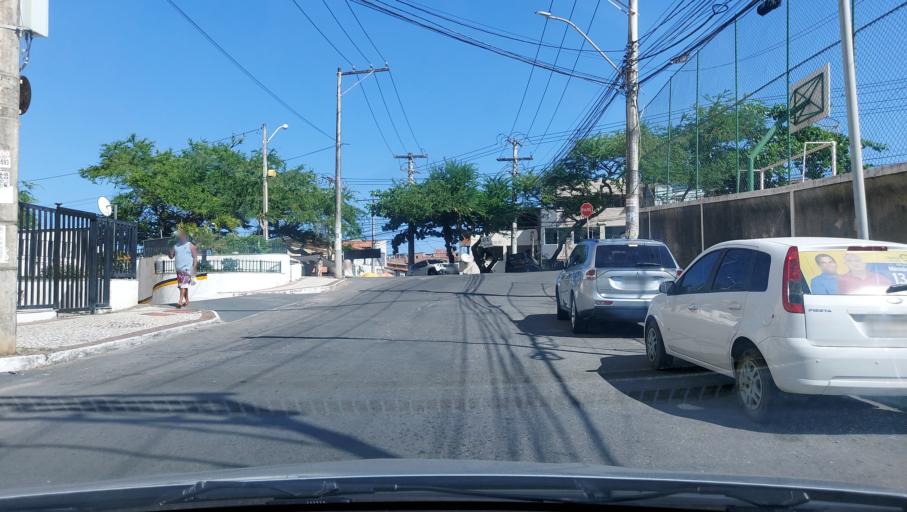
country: BR
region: Bahia
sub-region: Salvador
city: Salvador
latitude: -12.9746
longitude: -38.4349
